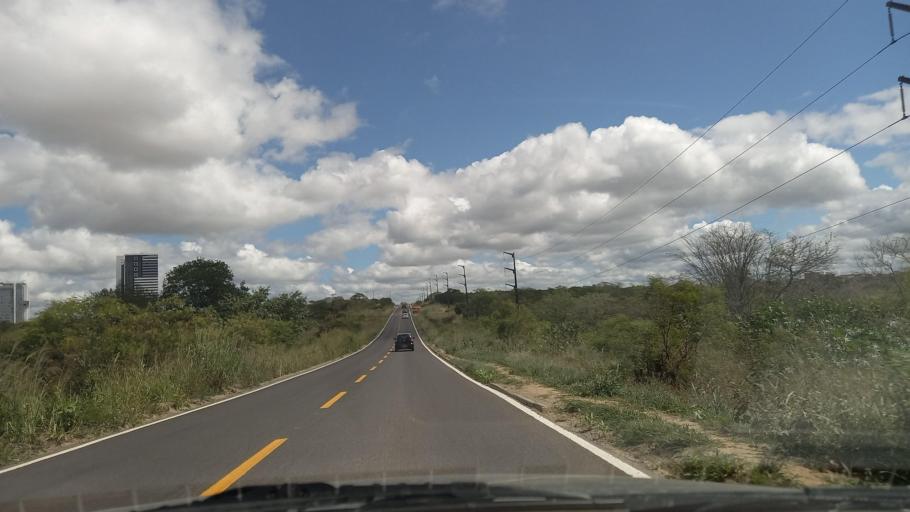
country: BR
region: Pernambuco
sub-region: Caruaru
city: Caruaru
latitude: -8.2570
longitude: -35.9583
